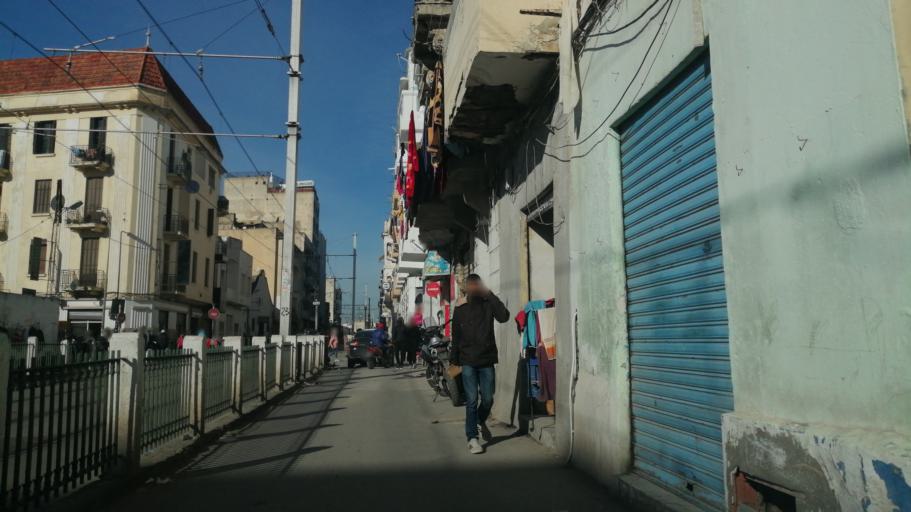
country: TN
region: Tunis
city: Tunis
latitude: 36.8089
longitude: 10.1780
